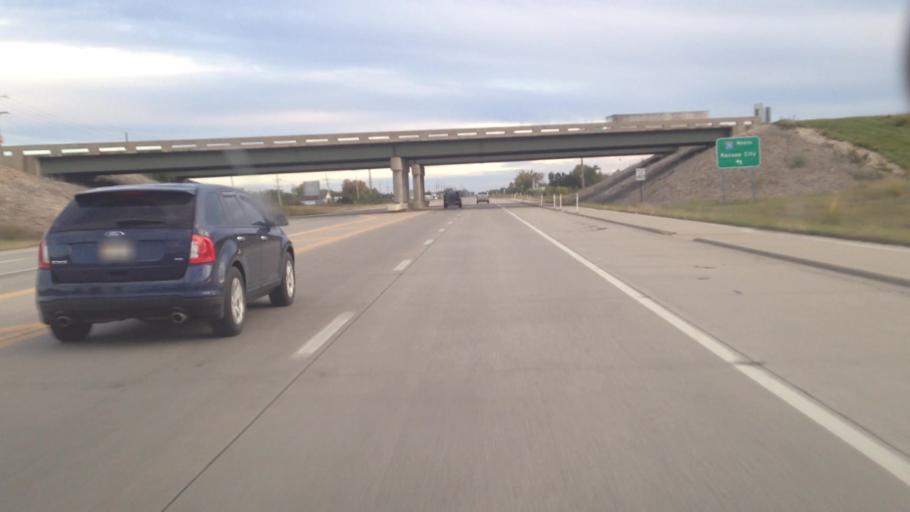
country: US
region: Kansas
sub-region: Franklin County
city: Ottawa
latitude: 38.5766
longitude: -95.2679
